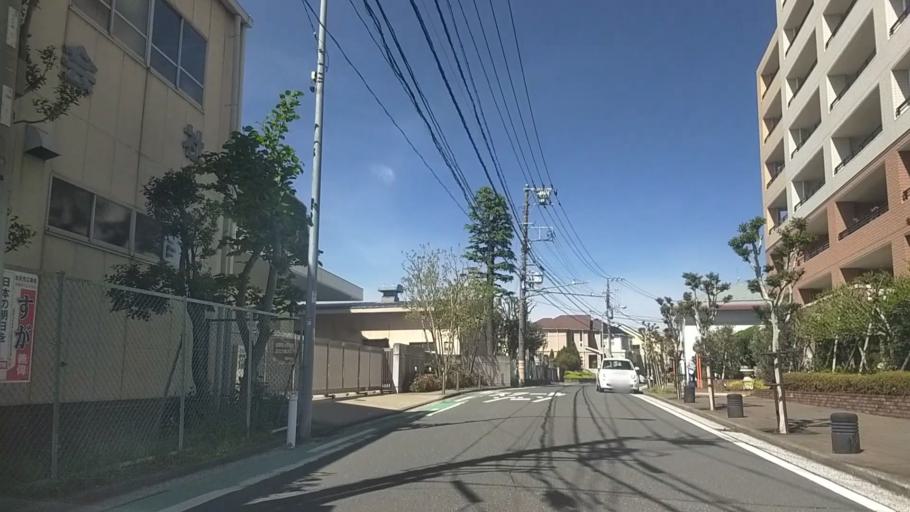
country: JP
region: Kanagawa
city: Yokohama
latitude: 35.4329
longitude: 139.6377
